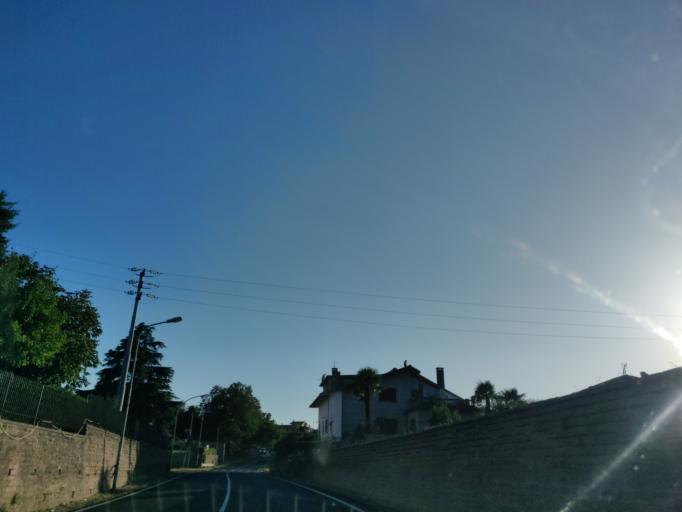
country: IT
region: Latium
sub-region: Provincia di Viterbo
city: Grotte di Castro
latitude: 42.6796
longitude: 11.8724
